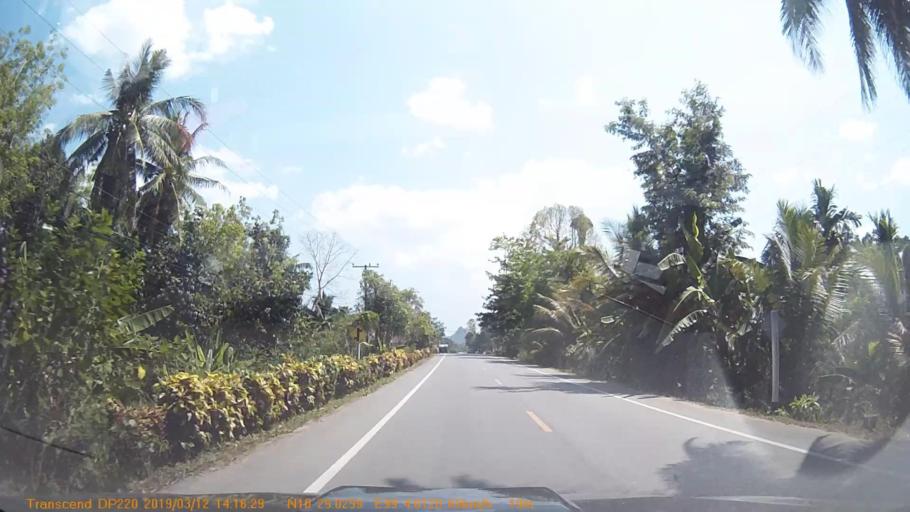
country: TH
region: Chumphon
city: Chumphon
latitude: 10.4835
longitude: 99.0769
